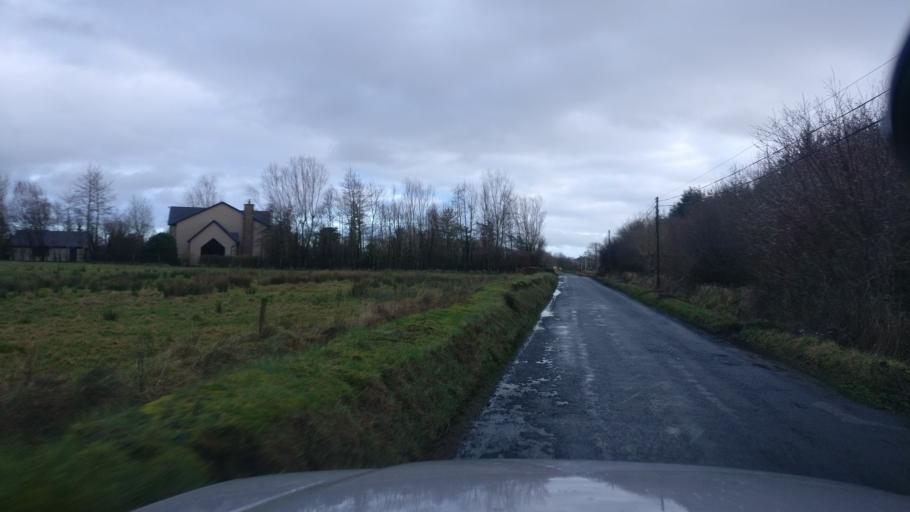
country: IE
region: Connaught
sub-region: County Galway
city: Athenry
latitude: 53.2969
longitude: -8.7022
